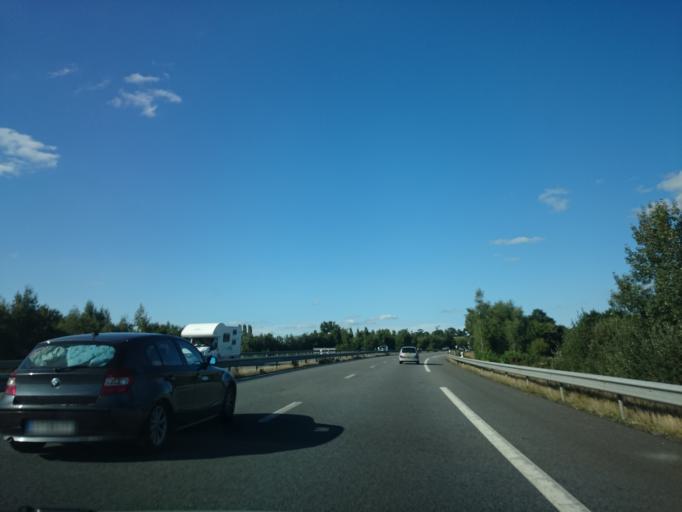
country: FR
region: Brittany
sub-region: Departement d'Ille-et-Vilaine
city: La Dominelais
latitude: 47.7815
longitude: -1.6993
